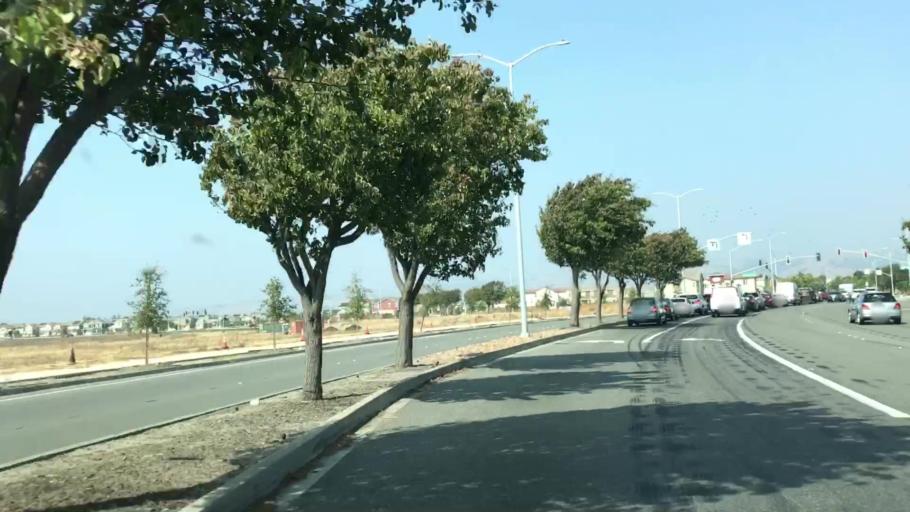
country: US
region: California
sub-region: Alameda County
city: Newark
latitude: 37.5595
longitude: -122.0654
